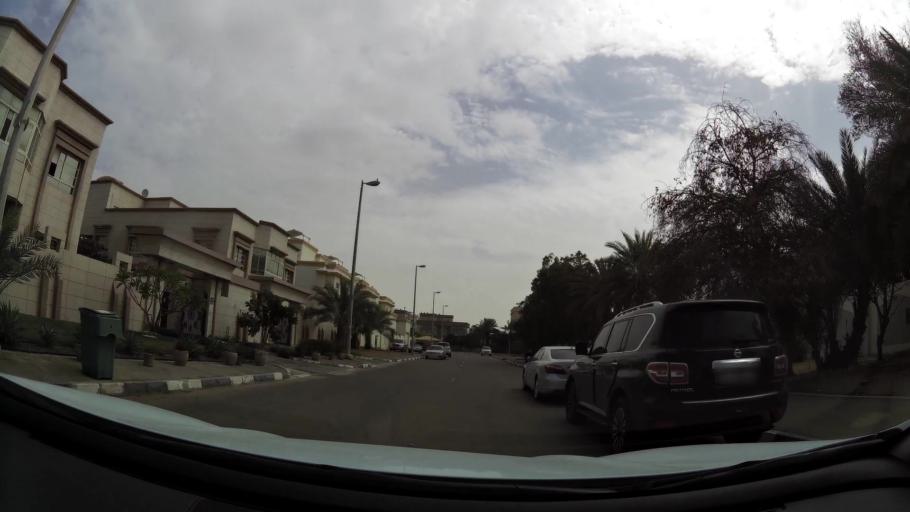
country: AE
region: Abu Dhabi
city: Abu Dhabi
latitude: 24.3936
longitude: 54.5036
